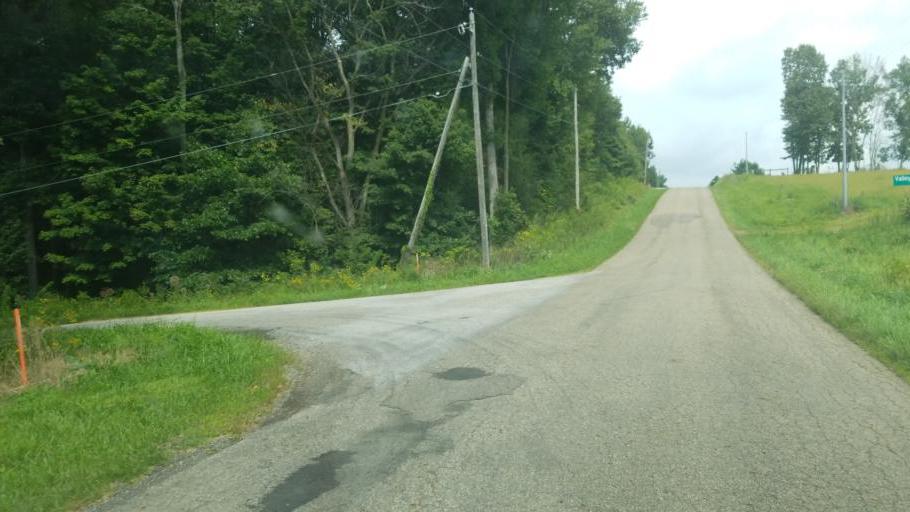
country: US
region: Ohio
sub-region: Knox County
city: Danville
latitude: 40.4615
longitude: -82.3268
